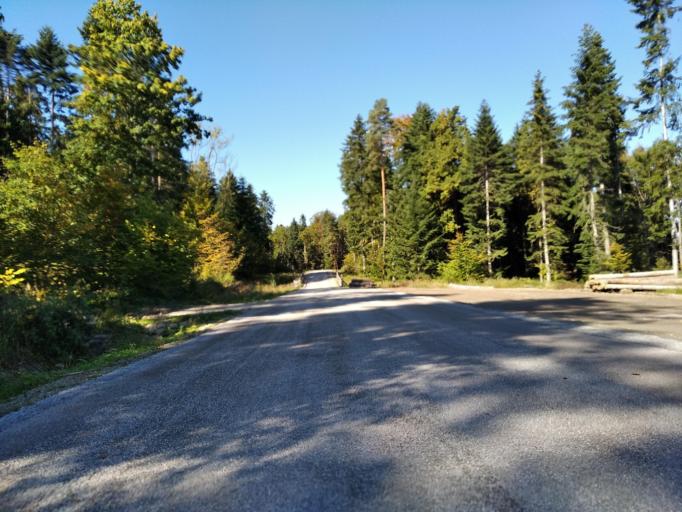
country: PL
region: Subcarpathian Voivodeship
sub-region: Powiat strzyzowski
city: Strzyzow
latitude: 49.8200
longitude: 21.8055
